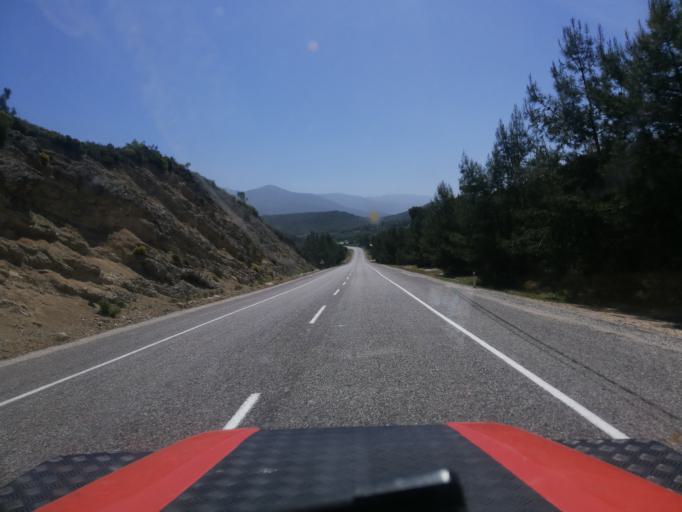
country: TR
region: Mugla
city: Esen
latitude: 36.3986
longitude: 29.3100
